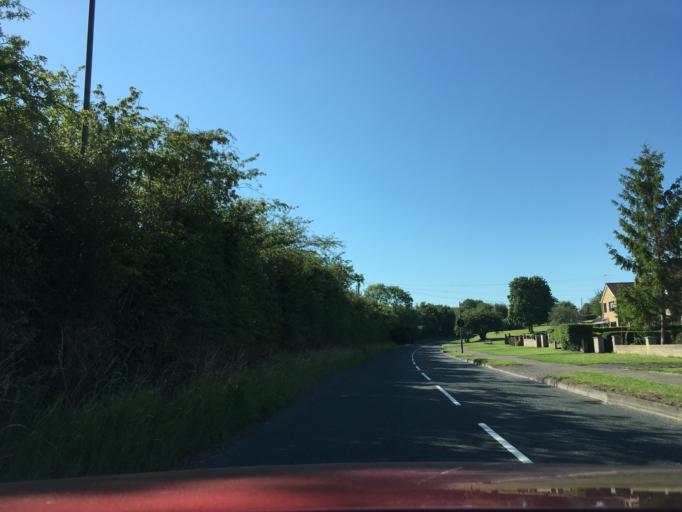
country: GB
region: England
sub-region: South Gloucestershire
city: Pucklechurch
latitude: 51.4846
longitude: -2.4296
